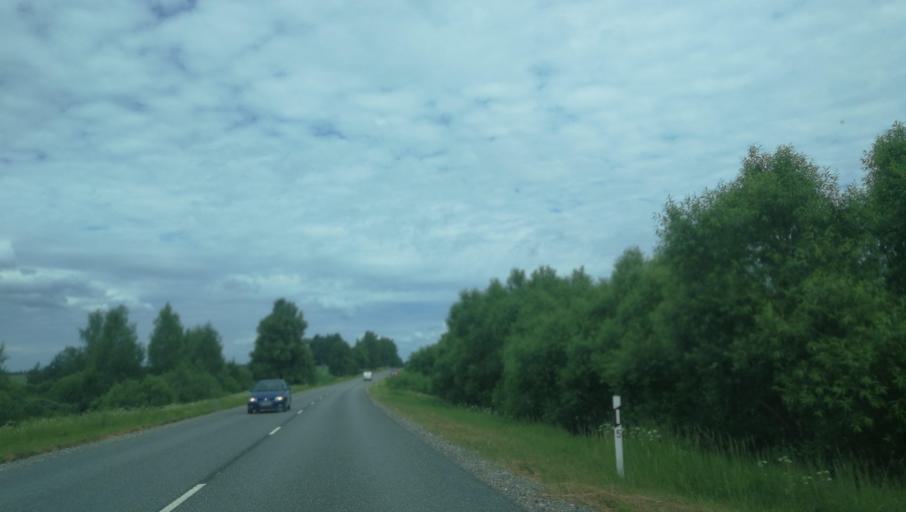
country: LV
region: Naukseni
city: Naukseni
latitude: 57.7308
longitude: 25.4232
